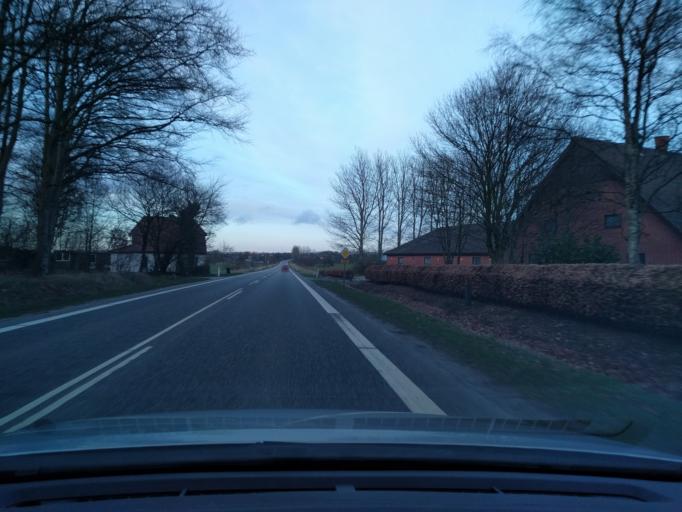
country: DK
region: South Denmark
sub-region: Tonder Kommune
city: Toftlund
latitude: 55.1378
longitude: 9.0073
